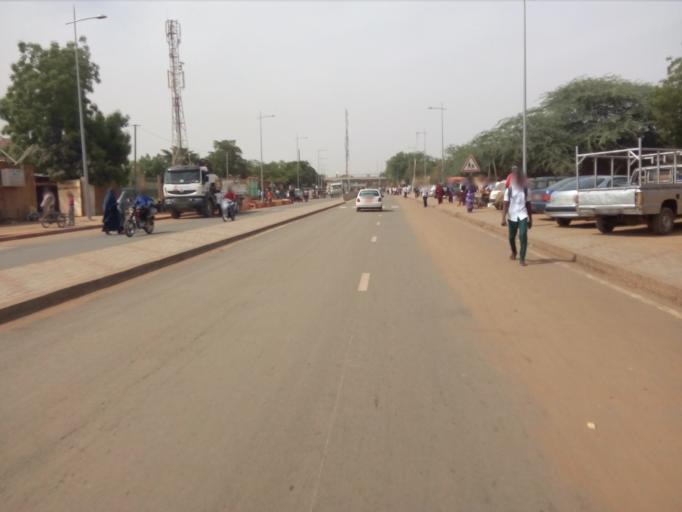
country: NE
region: Niamey
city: Niamey
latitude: 13.5234
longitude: 2.1201
